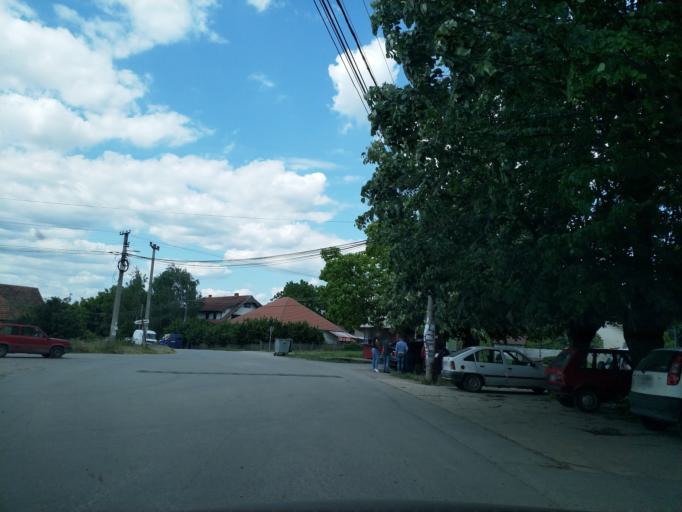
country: RS
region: Central Serbia
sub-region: Pomoravski Okrug
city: Jagodina
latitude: 43.9454
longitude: 21.2960
